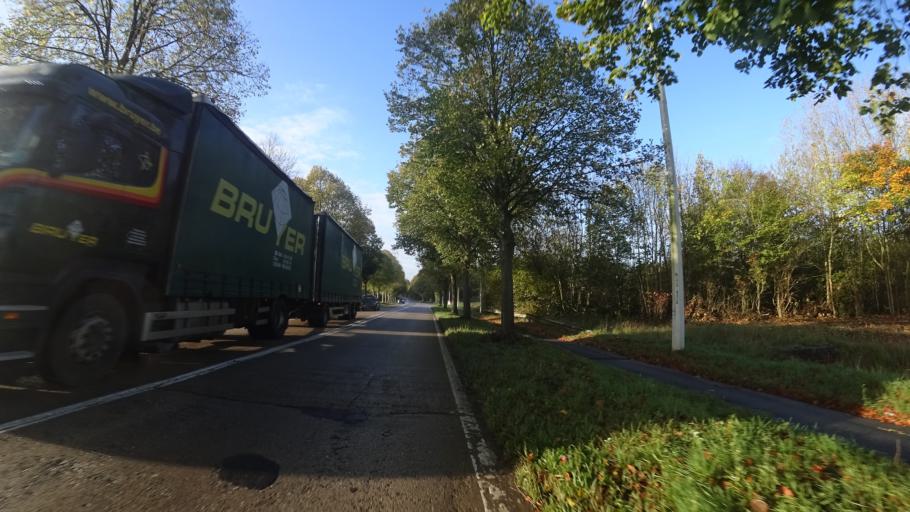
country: BE
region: Wallonia
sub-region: Province de Namur
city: Floreffe
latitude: 50.4820
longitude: 4.7872
